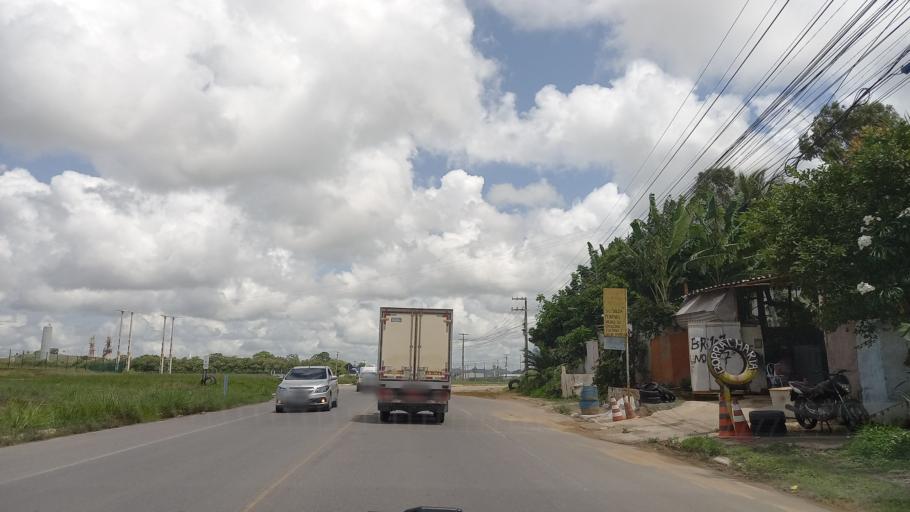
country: BR
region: Pernambuco
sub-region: Cabo De Santo Agostinho
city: Cabo
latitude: -8.2445
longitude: -34.9920
